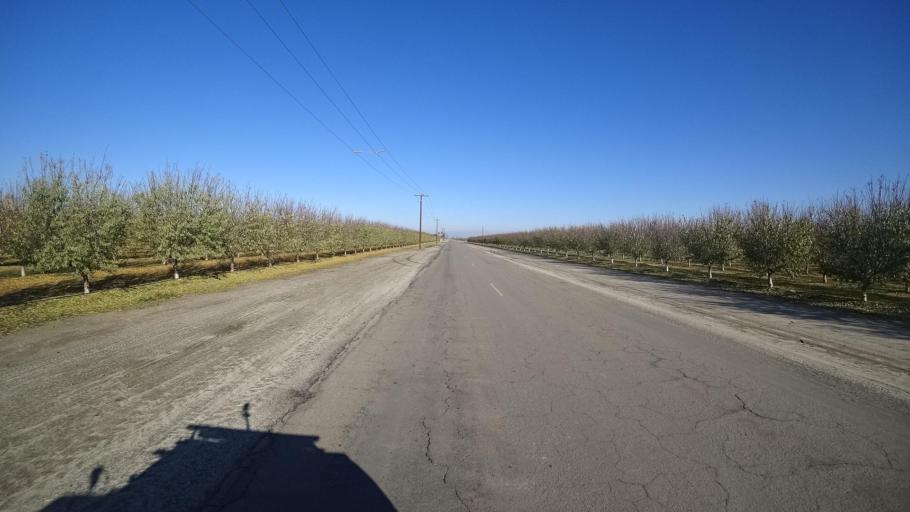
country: US
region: California
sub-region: Kern County
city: Delano
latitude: 35.7371
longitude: -119.2763
